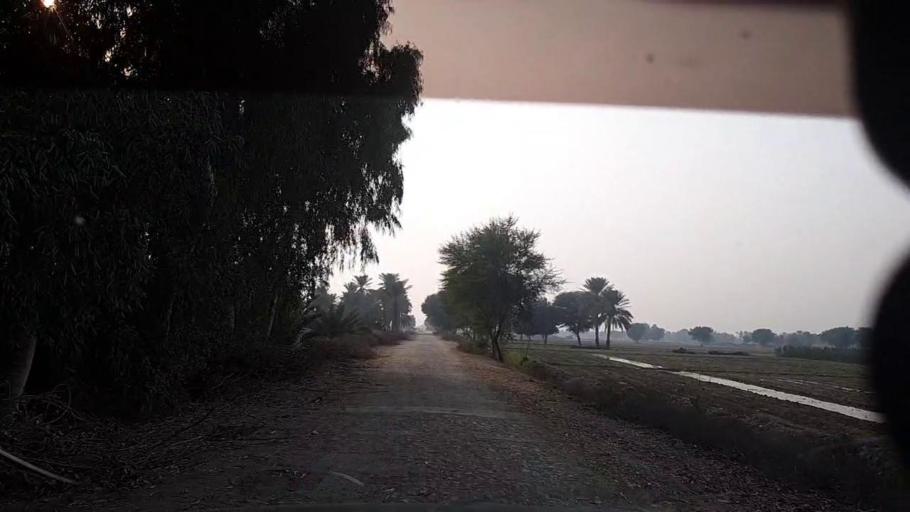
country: PK
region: Sindh
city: Kot Diji
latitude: 27.4375
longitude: 68.6275
